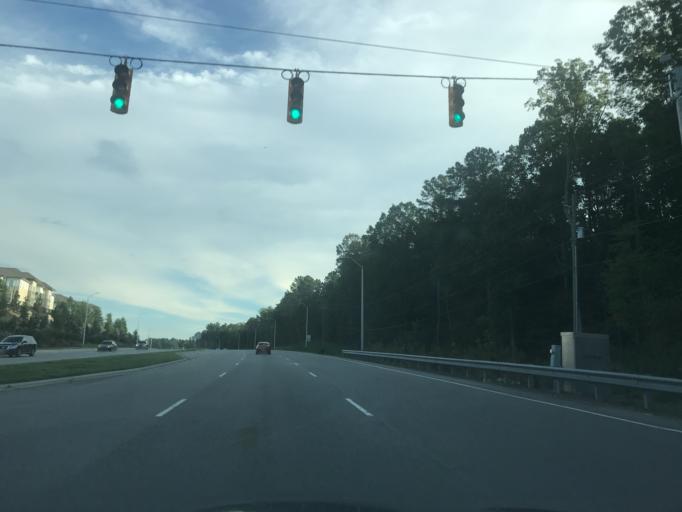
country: US
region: North Carolina
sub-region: Wake County
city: Green Level
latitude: 35.8514
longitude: -78.8943
